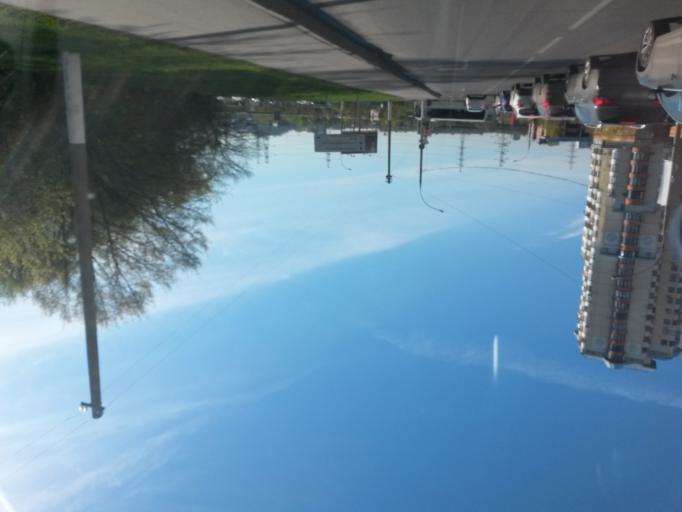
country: RU
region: Moscow
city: Annino
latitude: 55.5675
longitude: 37.5895
